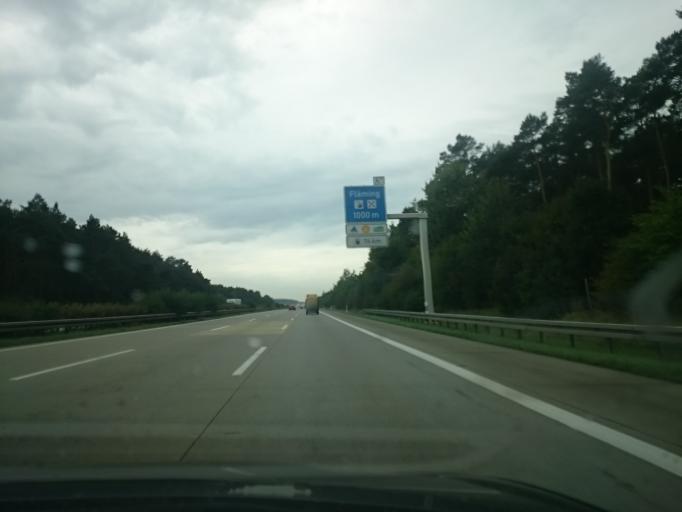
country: DE
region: Brandenburg
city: Linthe
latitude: 52.1446
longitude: 12.7657
